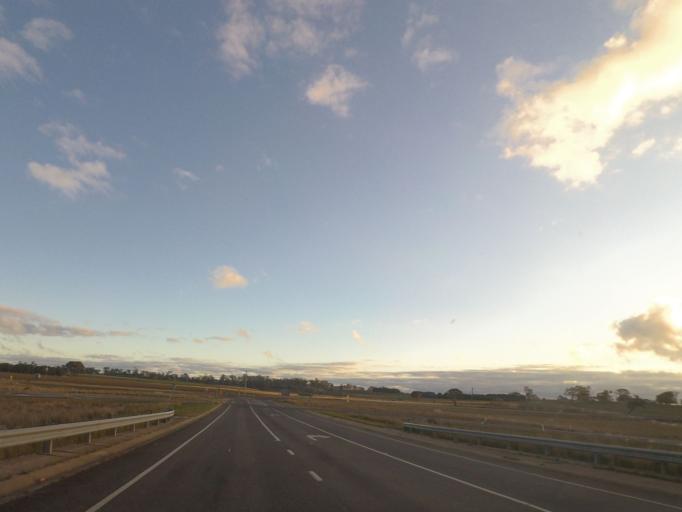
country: AU
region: Victoria
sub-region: Hume
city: Sunbury
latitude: -37.2956
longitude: 144.5015
